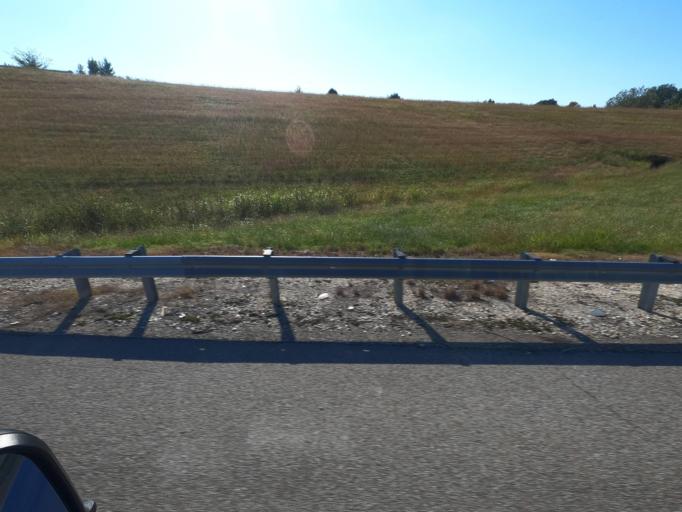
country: US
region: Tennessee
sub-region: Crockett County
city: Alamo
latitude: 35.8127
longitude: -89.1614
